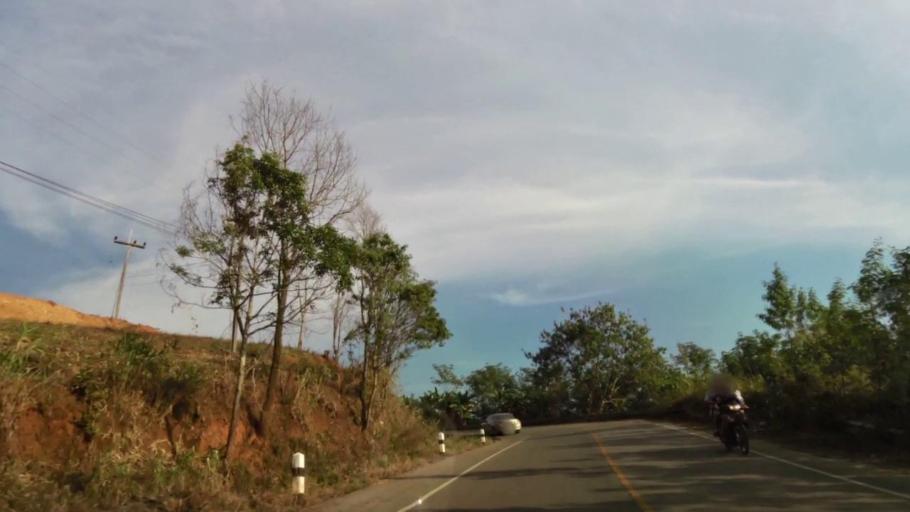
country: TH
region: Chiang Rai
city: Khun Tan
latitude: 19.8668
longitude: 100.4106
